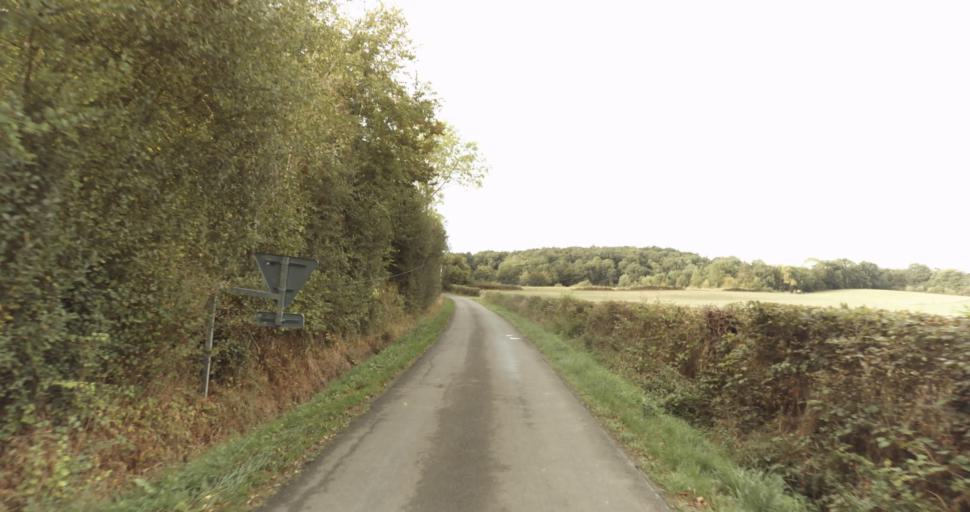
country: FR
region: Lower Normandy
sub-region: Departement de l'Orne
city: Sees
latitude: 48.6833
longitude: 0.2486
